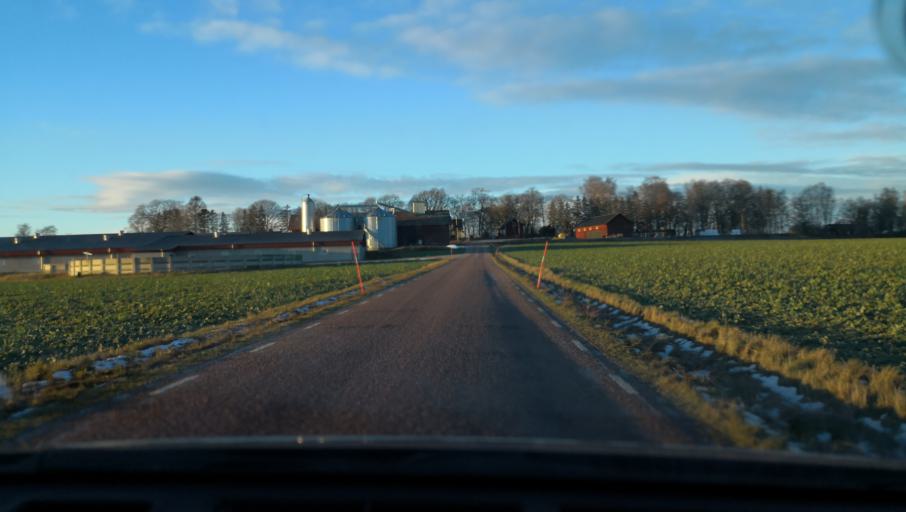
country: SE
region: Vaestmanland
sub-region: Vasteras
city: Hokasen
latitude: 59.7000
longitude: 16.5844
